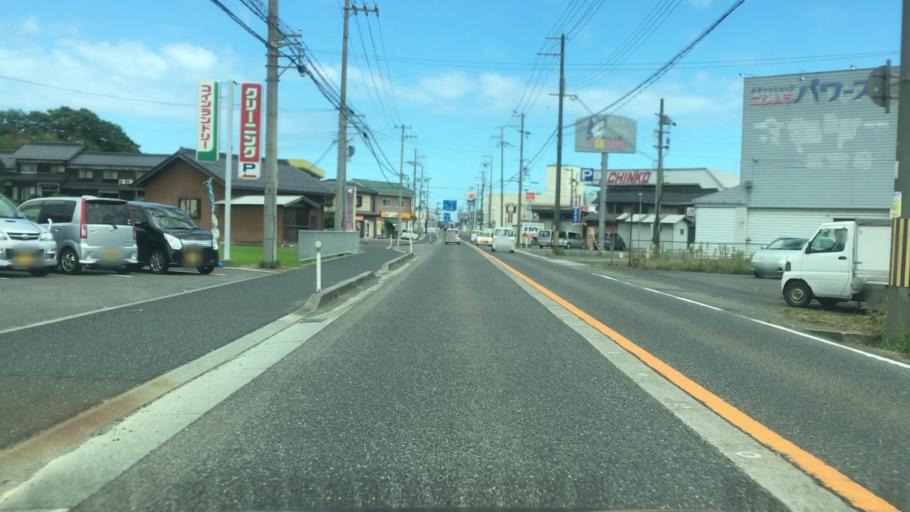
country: JP
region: Tottori
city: Tottori
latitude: 35.6175
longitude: 134.4633
